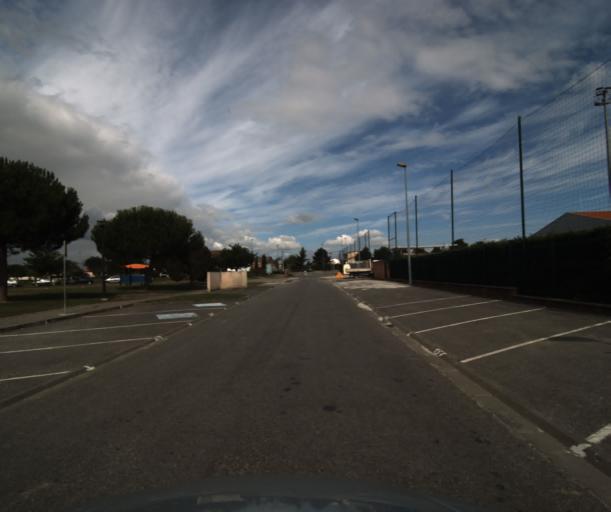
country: FR
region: Midi-Pyrenees
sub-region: Departement de la Haute-Garonne
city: Muret
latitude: 43.4668
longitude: 1.3197
